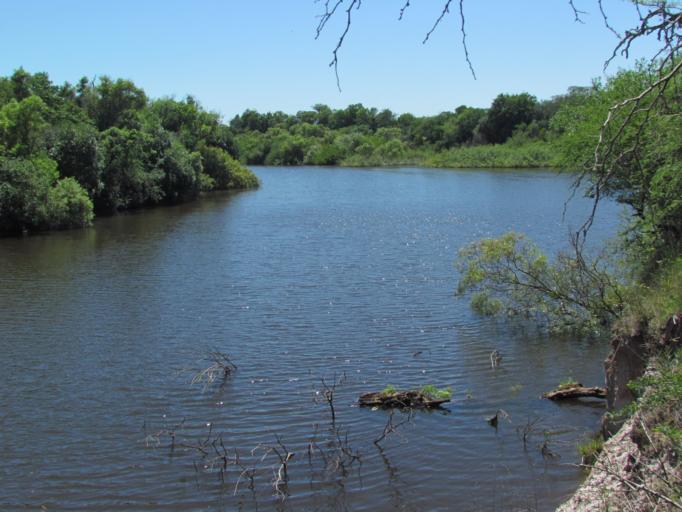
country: AR
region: Entre Rios
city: Concepcion del Uruguay
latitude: -32.4745
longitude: -58.0950
